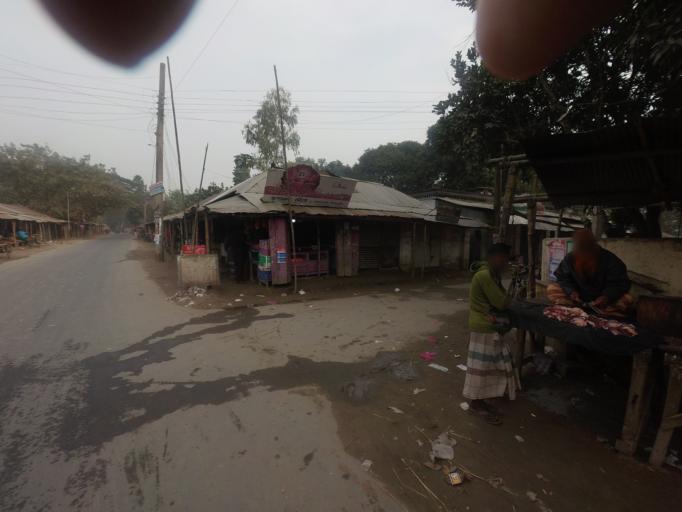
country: BD
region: Rajshahi
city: Saidpur
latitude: 25.9507
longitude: 88.9053
